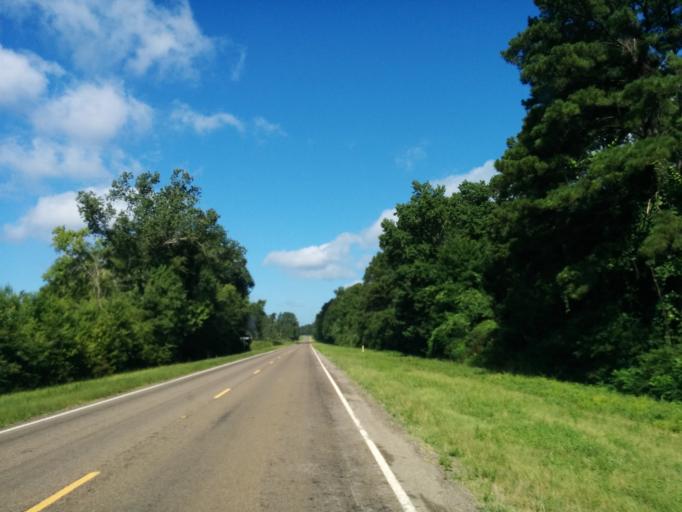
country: US
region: Texas
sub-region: San Augustine County
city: San Augustine
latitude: 31.4110
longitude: -94.0161
